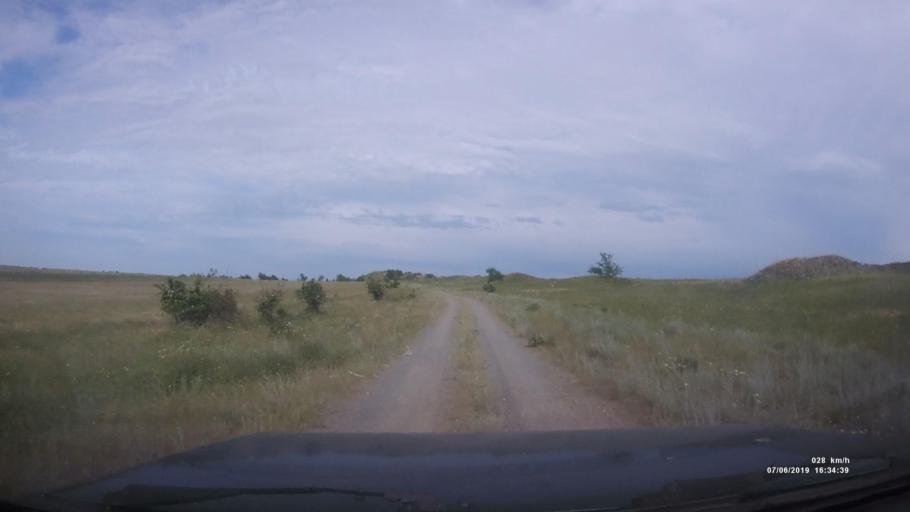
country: RU
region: Rostov
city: Staraya Stanitsa
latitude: 48.2511
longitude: 40.3428
